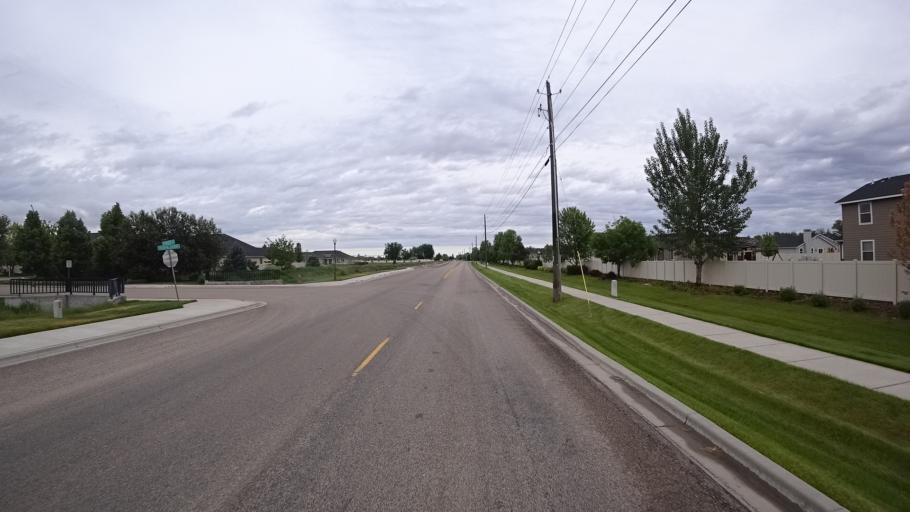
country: US
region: Idaho
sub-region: Ada County
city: Star
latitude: 43.7065
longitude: -116.4772
